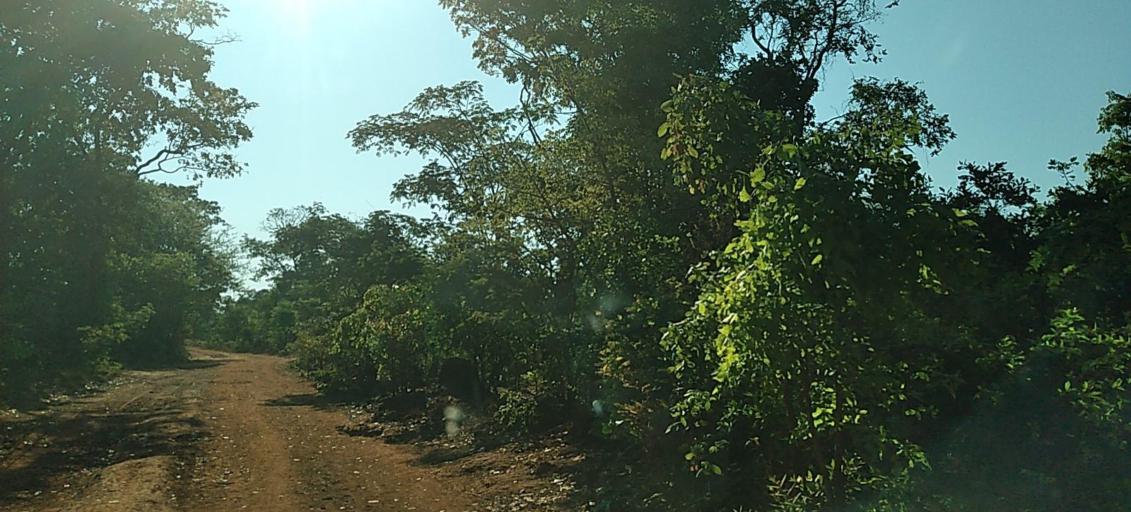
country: ZM
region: Copperbelt
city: Luanshya
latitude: -13.4591
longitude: 28.8160
